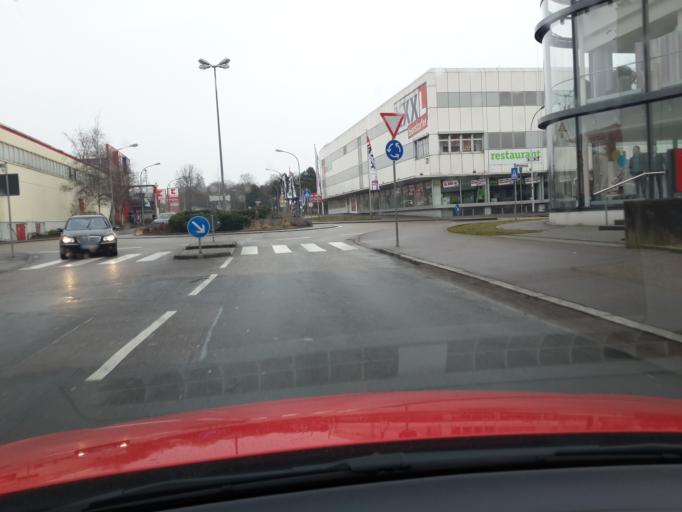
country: DE
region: Baden-Wuerttemberg
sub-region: Regierungsbezirk Stuttgart
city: Heilbronn
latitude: 49.1505
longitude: 9.1969
